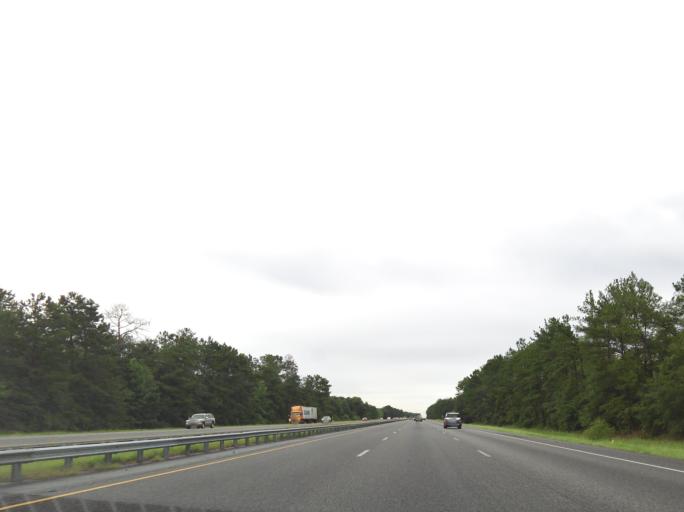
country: US
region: Georgia
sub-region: Lowndes County
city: Valdosta
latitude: 30.7162
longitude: -83.2537
